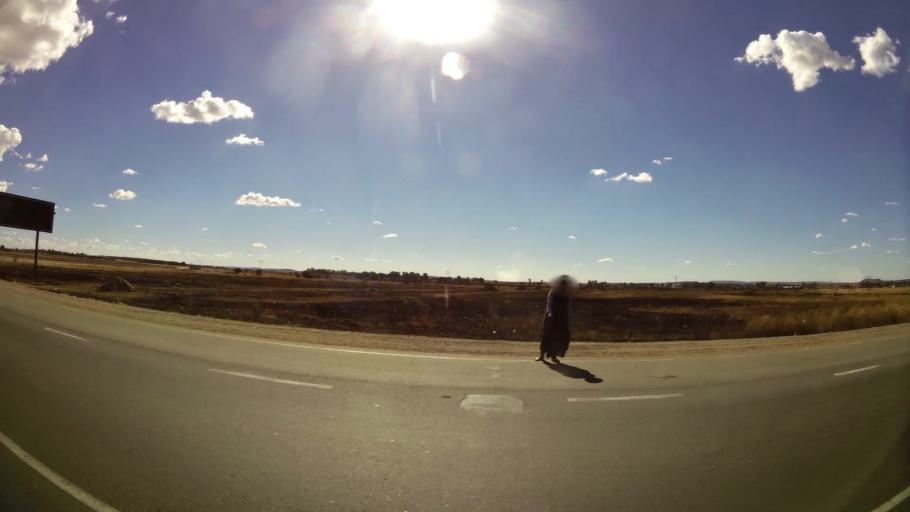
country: ZA
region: North-West
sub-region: Dr Kenneth Kaunda District Municipality
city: Klerksdorp
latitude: -26.8721
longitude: 26.6115
